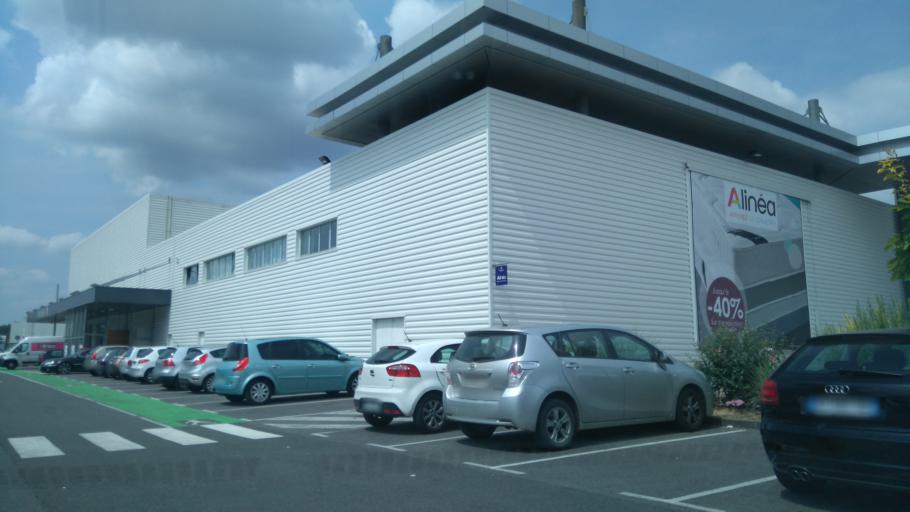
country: FR
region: Picardie
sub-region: Departement de l'Oise
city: Saint-Maximin
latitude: 49.2368
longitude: 2.4659
